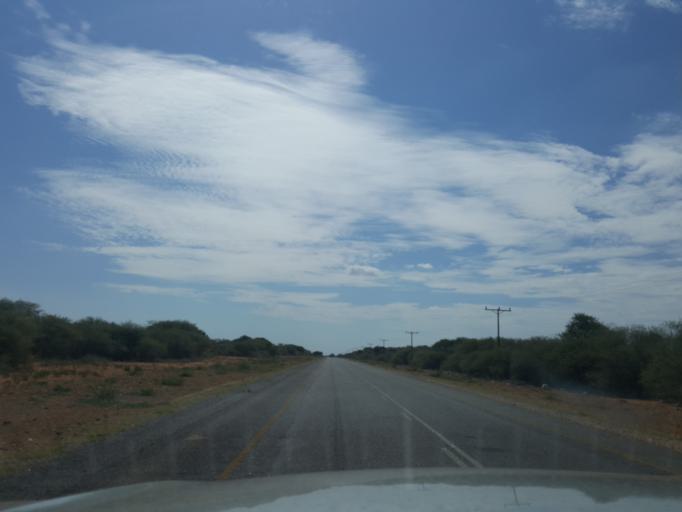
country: BW
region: Kweneng
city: Letlhakeng
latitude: -24.1440
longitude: 25.1484
